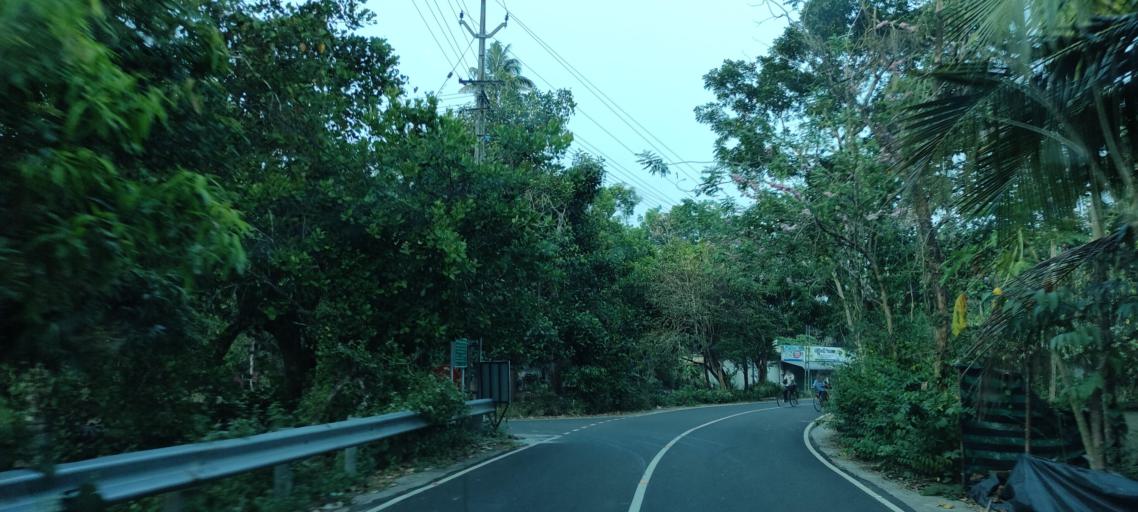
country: IN
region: Kerala
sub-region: Alappuzha
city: Mavelikara
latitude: 9.2771
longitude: 76.5593
